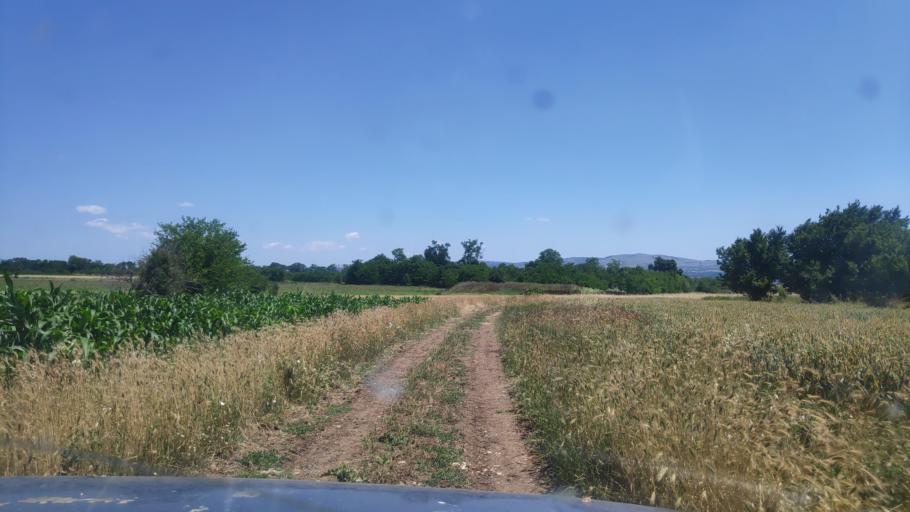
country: MK
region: Kumanovo
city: Bedinje
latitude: 42.1676
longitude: 21.6848
